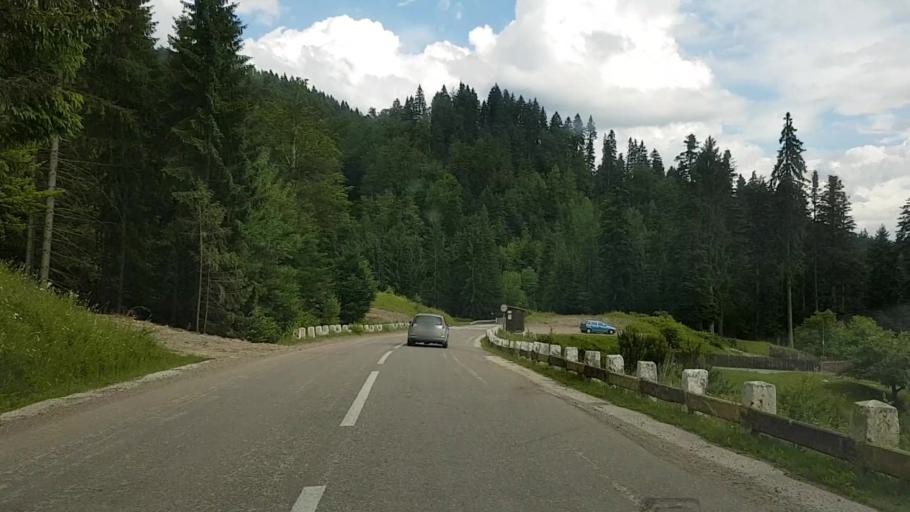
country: RO
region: Neamt
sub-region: Comuna Pangarati
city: Pangarati
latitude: 46.9770
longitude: 26.1157
